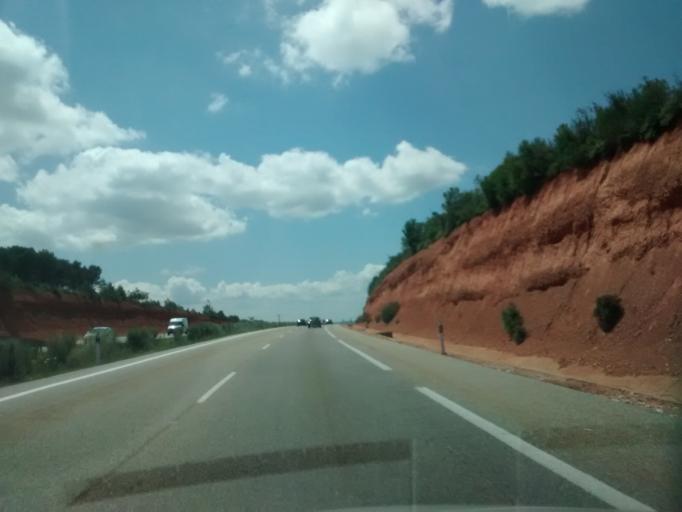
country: ES
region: Castille and Leon
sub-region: Provincia de Leon
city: Brazuelo
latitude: 42.5082
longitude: -6.1172
